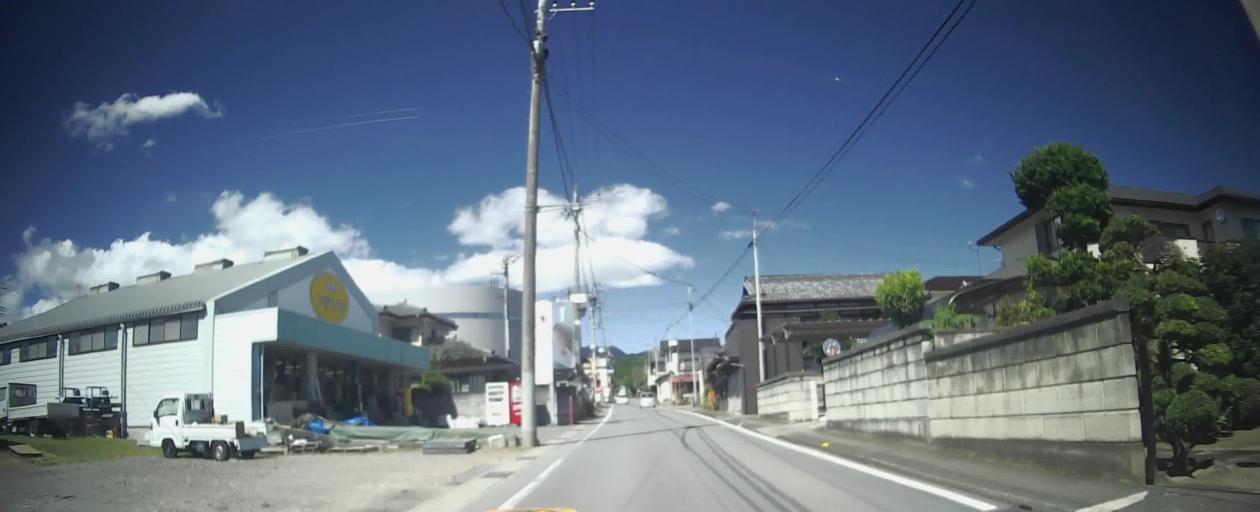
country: JP
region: Gunma
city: Kanekomachi
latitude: 36.3946
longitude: 138.9563
